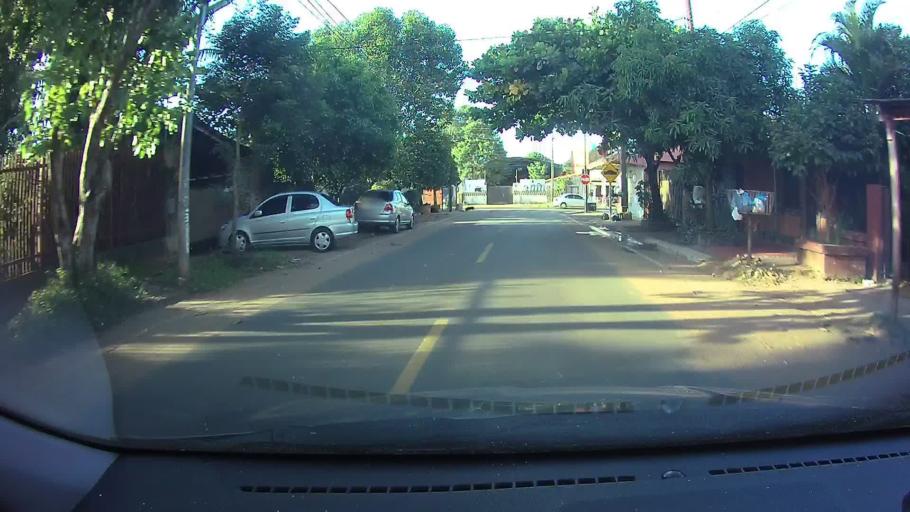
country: PY
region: Central
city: San Lorenzo
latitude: -25.2751
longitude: -57.4814
